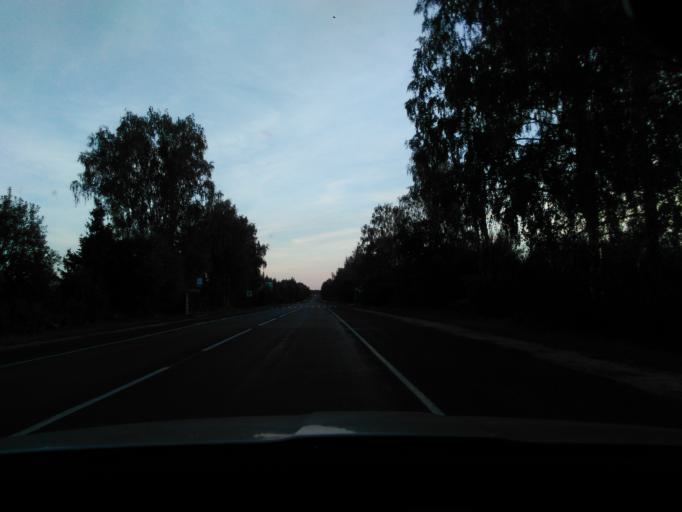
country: RU
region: Tverskaya
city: Zavidovo
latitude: 56.6026
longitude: 36.6235
